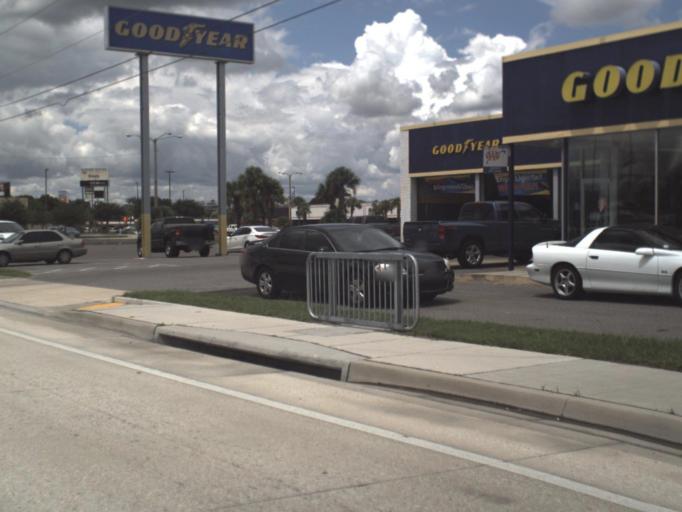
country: US
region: Florida
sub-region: Polk County
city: Bartow
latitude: 27.9041
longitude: -81.8406
